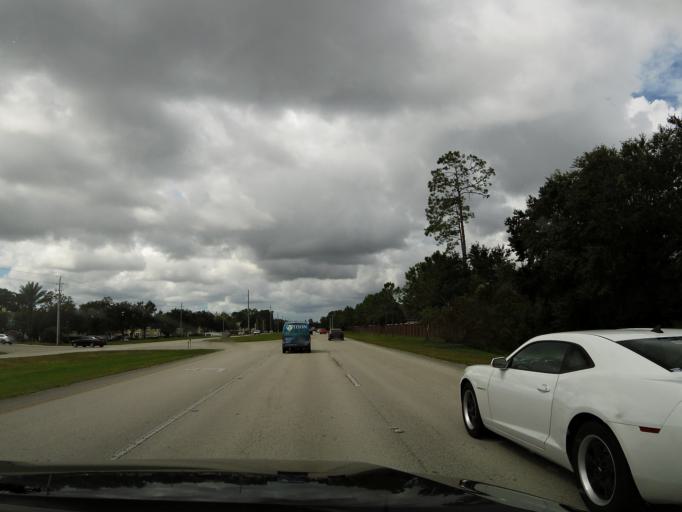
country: US
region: Florida
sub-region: Clay County
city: Lakeside
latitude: 30.1023
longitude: -81.7226
